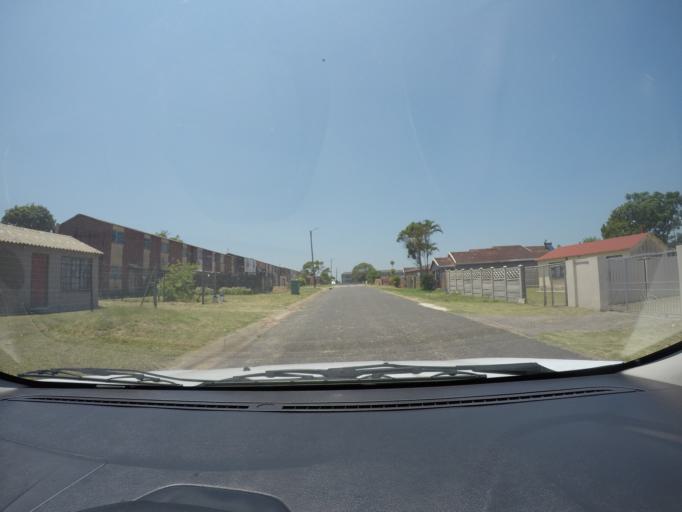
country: ZA
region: KwaZulu-Natal
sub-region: uThungulu District Municipality
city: eSikhawini
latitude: -28.8849
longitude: 31.8899
